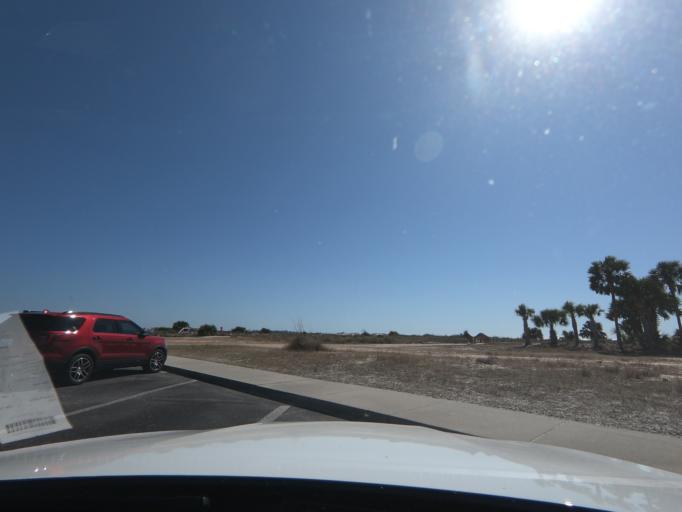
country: US
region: Florida
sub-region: Bay County
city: Lower Grand Lagoon
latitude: 30.1252
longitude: -85.7334
